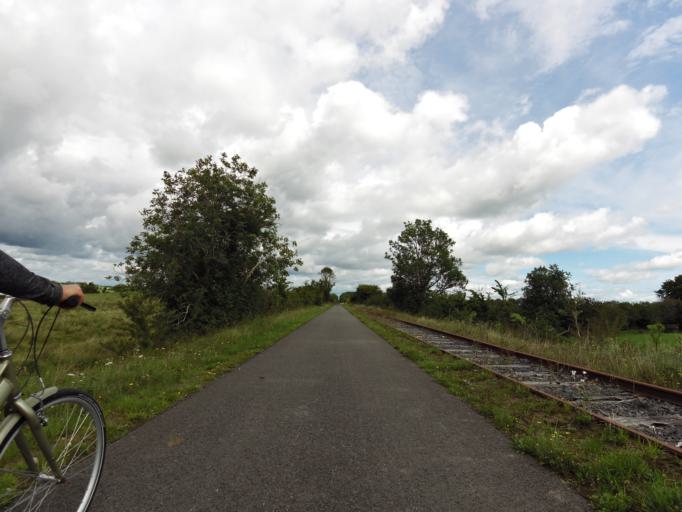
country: IE
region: Leinster
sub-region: An Iarmhi
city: Kilbeggan
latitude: 53.4797
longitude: -7.4750
